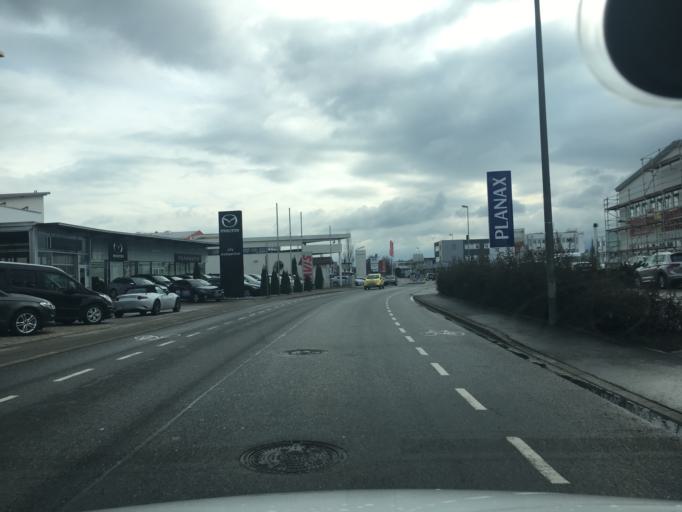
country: DE
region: Bavaria
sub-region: Upper Bavaria
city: Kolbermoor
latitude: 47.8492
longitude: 12.0785
